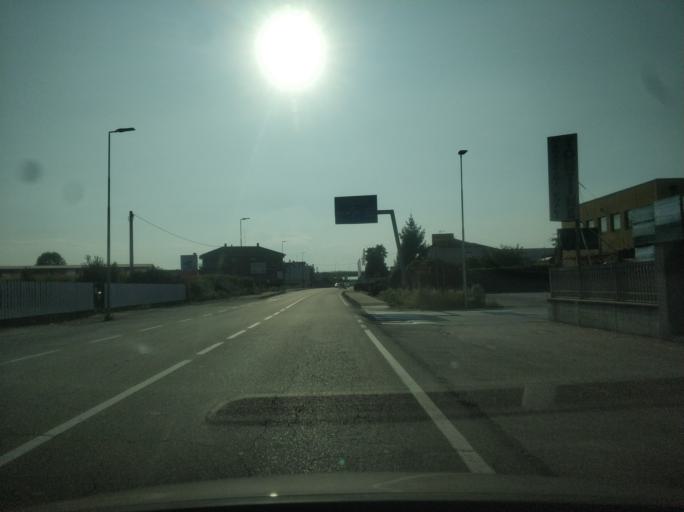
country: IT
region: Piedmont
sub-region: Provincia di Cuneo
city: Roreto
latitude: 44.6678
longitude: 7.8288
